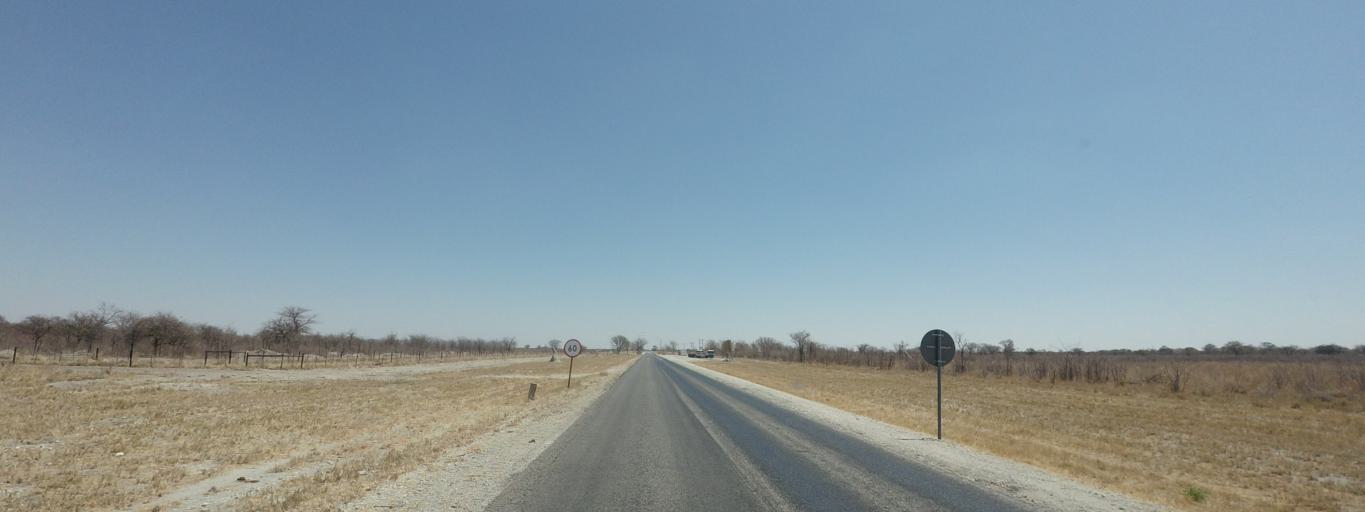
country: BW
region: Central
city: Nata
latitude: -20.3176
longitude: 26.3089
